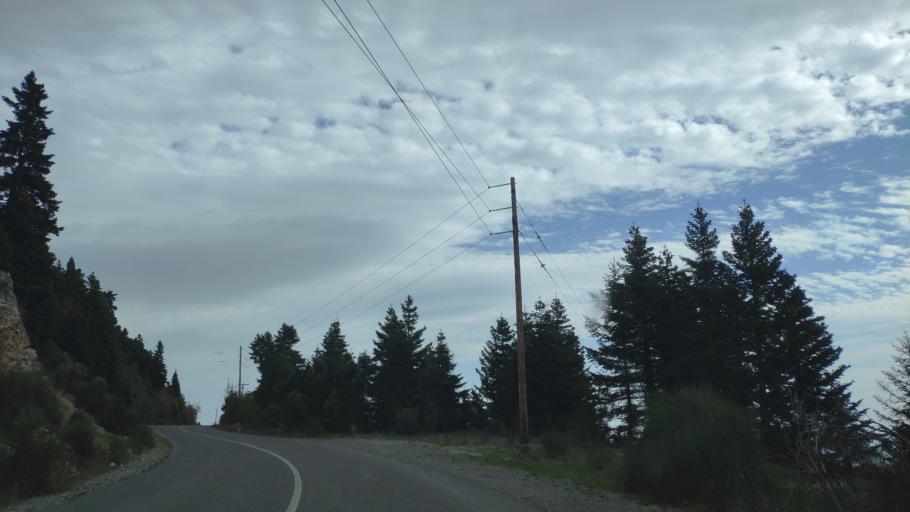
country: GR
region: Central Greece
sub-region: Nomos Fokidos
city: Amfissa
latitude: 38.7026
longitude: 22.3189
